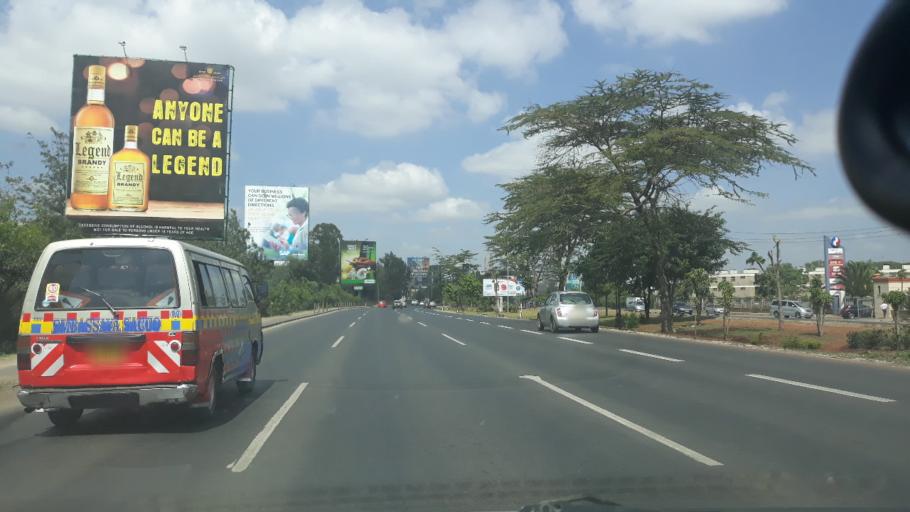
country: KE
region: Nairobi Area
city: Pumwani
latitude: -1.3173
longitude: 36.8342
